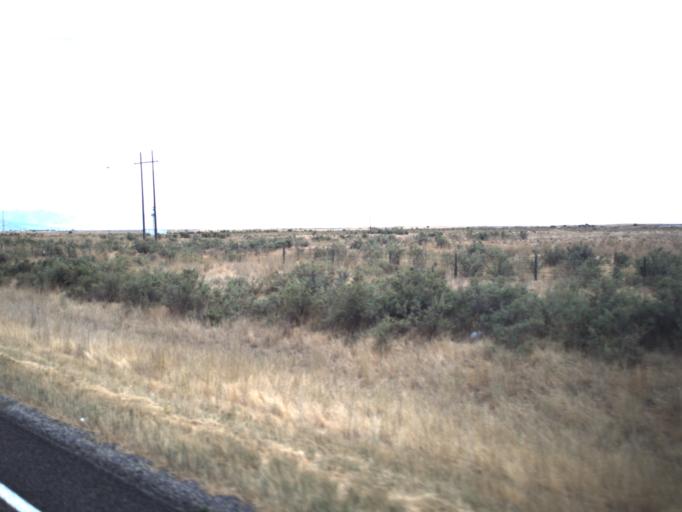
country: US
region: Utah
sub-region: Box Elder County
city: Tremonton
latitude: 41.5913
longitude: -112.2763
